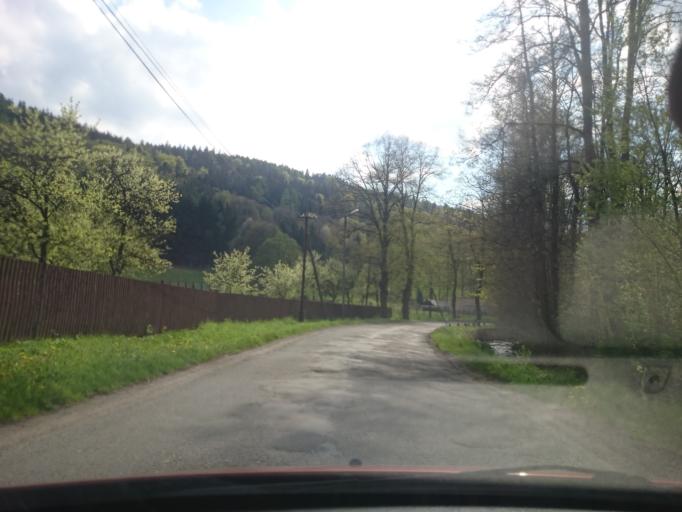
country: PL
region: Lower Silesian Voivodeship
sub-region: Powiat klodzki
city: Bystrzyca Klodzka
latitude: 50.3045
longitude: 16.6046
